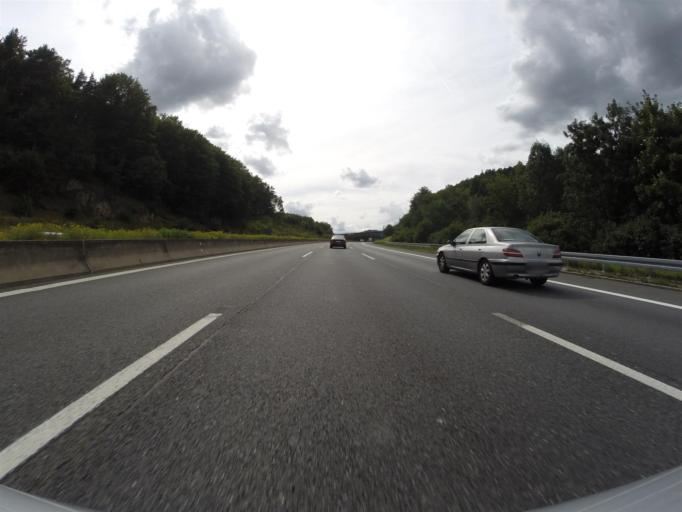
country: DE
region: Bavaria
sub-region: Regierungsbezirk Mittelfranken
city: Velden
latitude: 49.6506
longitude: 11.4480
